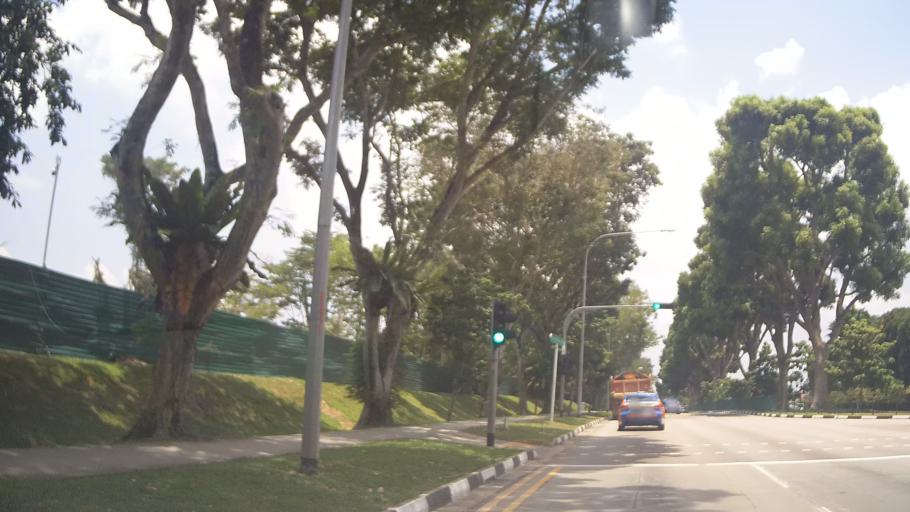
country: MY
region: Johor
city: Kampung Pasir Gudang Baru
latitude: 1.3898
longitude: 103.8636
